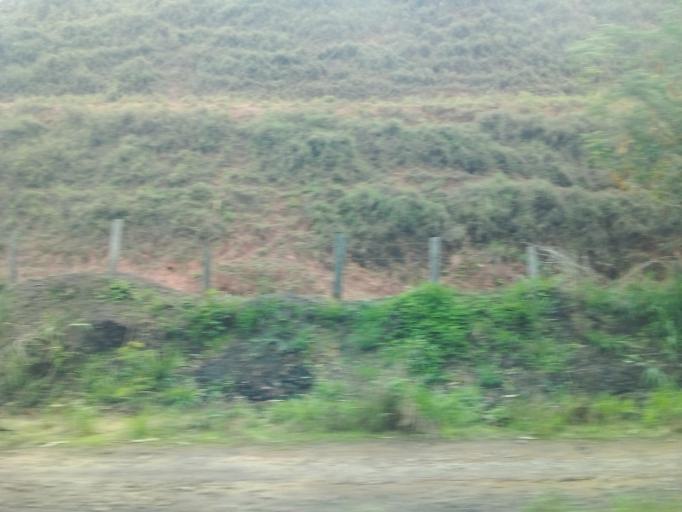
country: BR
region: Minas Gerais
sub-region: Governador Valadares
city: Governador Valadares
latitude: -19.0732
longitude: -42.1535
